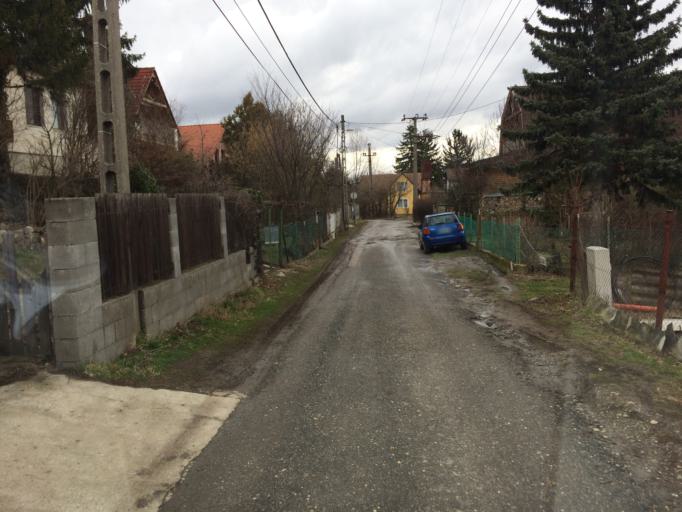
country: HU
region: Pest
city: Leanyfalu
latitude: 47.7246
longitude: 19.0751
